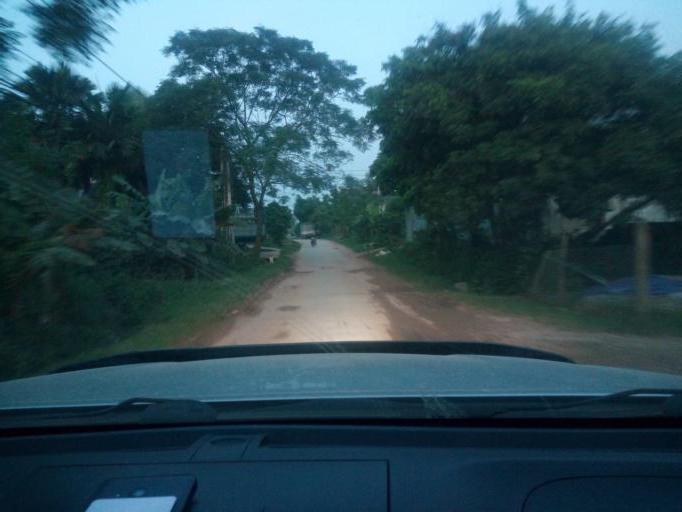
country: VN
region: Yen Bai
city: Co Phuc
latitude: 21.8609
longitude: 104.6352
